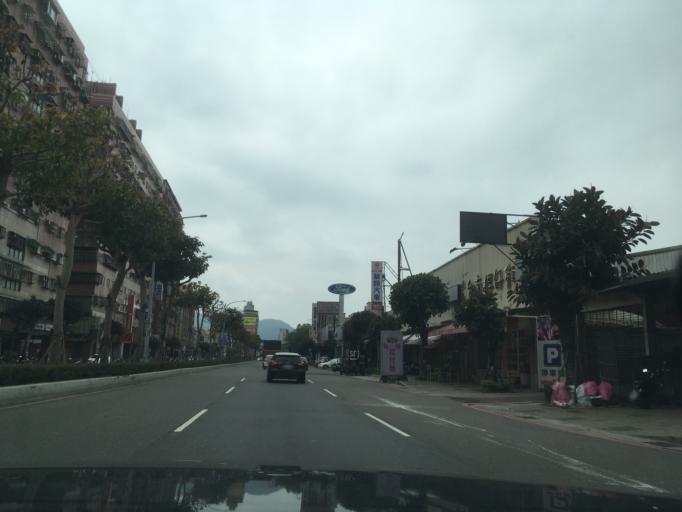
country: TW
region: Taipei
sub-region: Taipei
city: Banqiao
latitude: 24.9819
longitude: 121.4409
